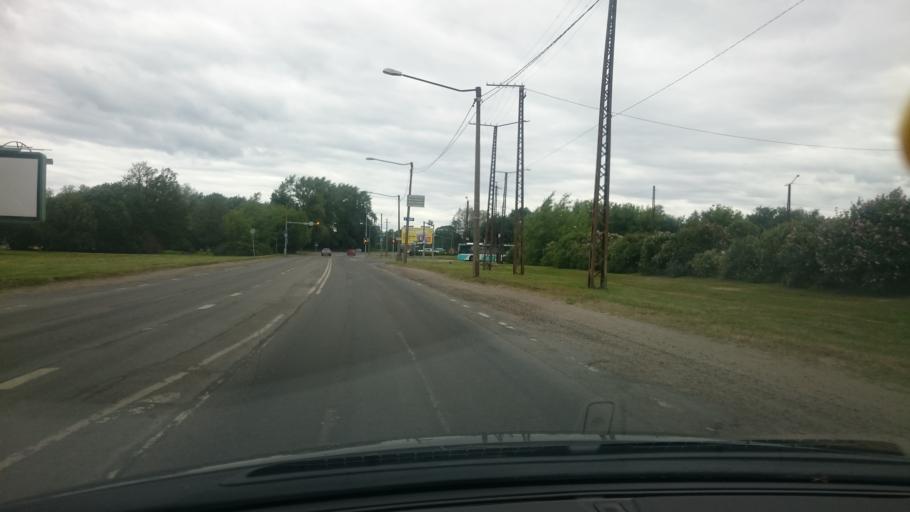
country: EE
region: Harju
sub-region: Saue vald
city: Laagri
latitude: 59.4125
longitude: 24.6338
